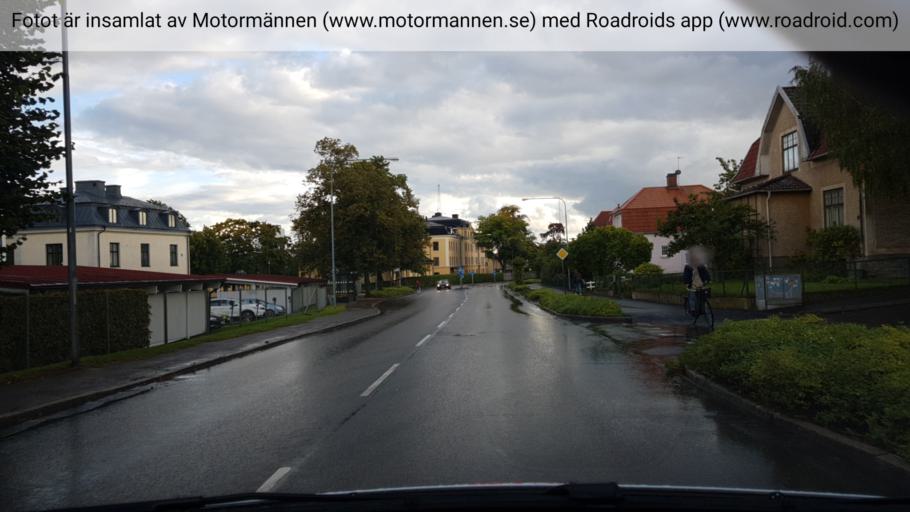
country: SE
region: Vaestra Goetaland
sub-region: Skovde Kommun
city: Skoevde
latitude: 58.3974
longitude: 13.8548
